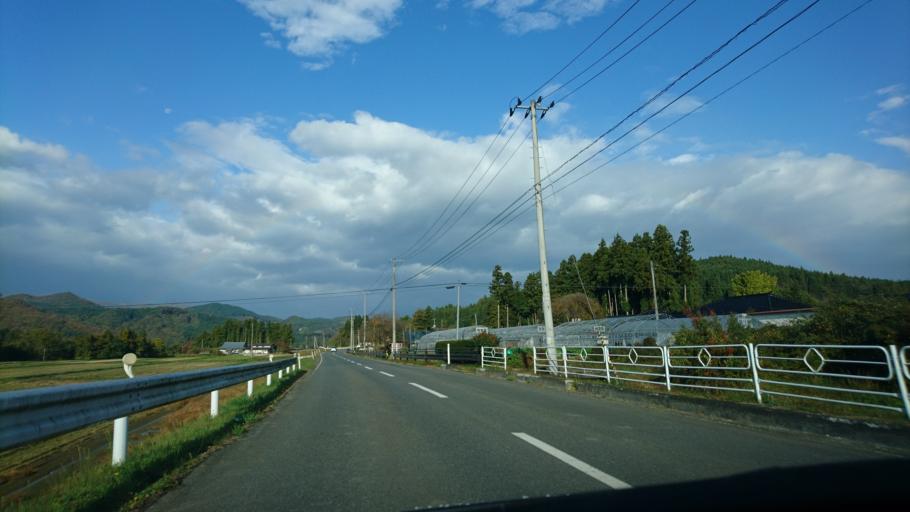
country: JP
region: Iwate
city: Mizusawa
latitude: 39.0450
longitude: 141.0587
